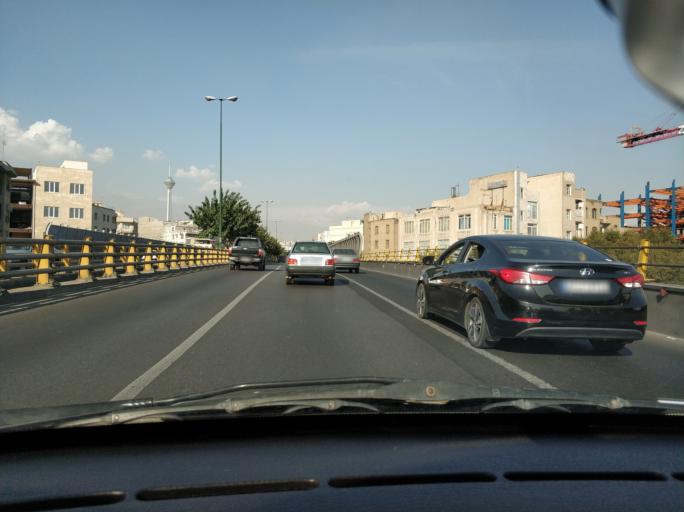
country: IR
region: Tehran
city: Tehran
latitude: 35.7201
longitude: 51.3596
